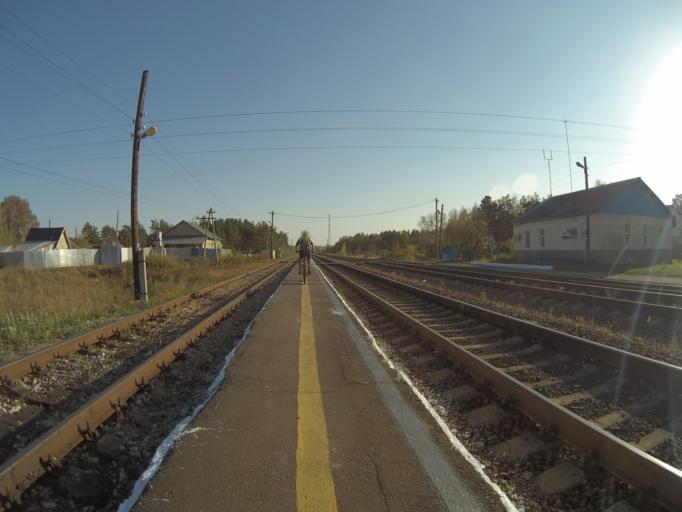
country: RU
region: Vladimir
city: Raduzhnyy
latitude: 56.0284
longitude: 40.3846
